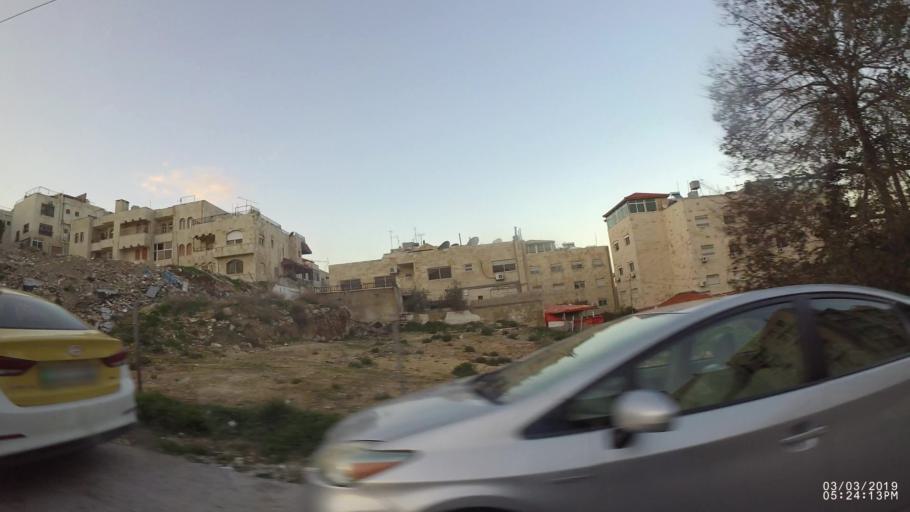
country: JO
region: Amman
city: Al Jubayhah
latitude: 31.9858
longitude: 35.8834
